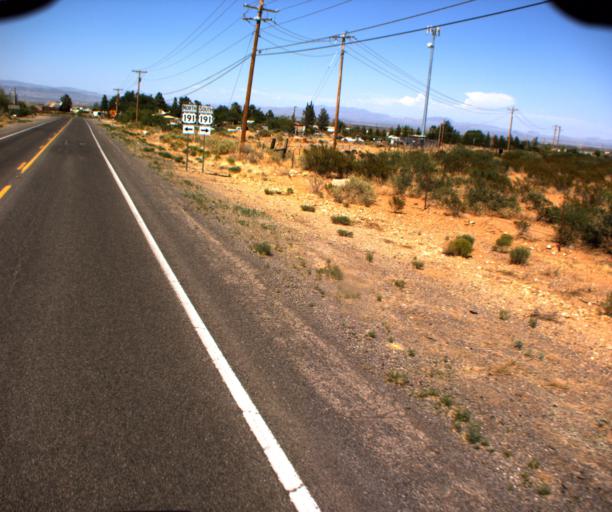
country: US
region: Arizona
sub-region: Graham County
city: Swift Trail Junction
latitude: 32.7278
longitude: -109.7163
